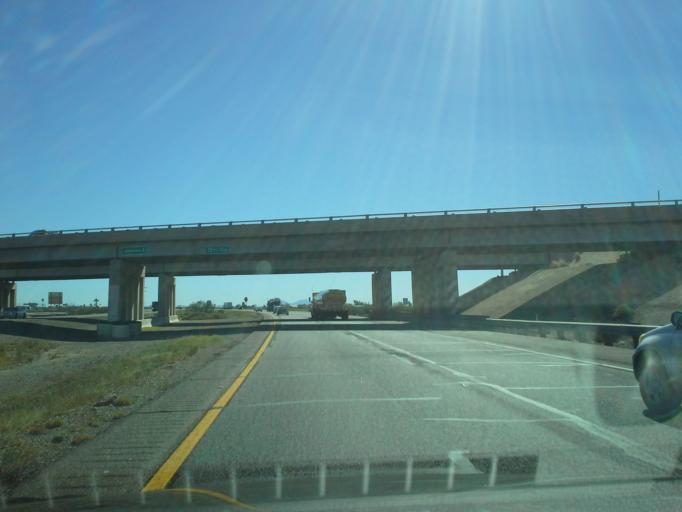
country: US
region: Arizona
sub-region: Pinal County
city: Arizona City
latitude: 32.8200
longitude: -111.6839
